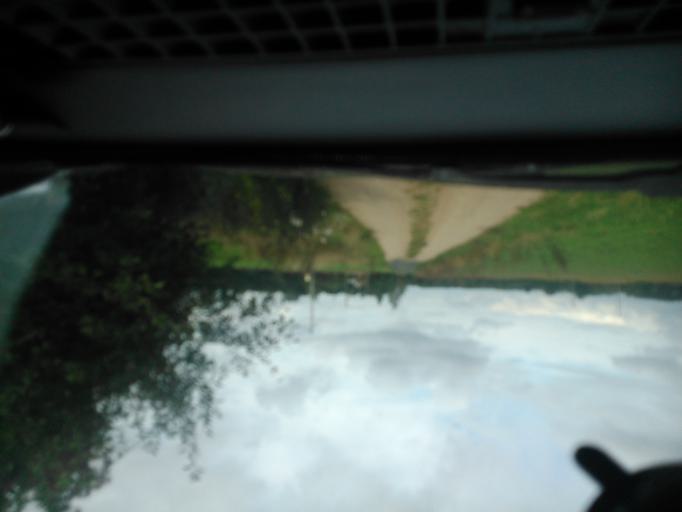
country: PL
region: Kujawsko-Pomorskie
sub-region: Powiat brodnicki
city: Swiedziebnia
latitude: 53.1877
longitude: 19.5348
